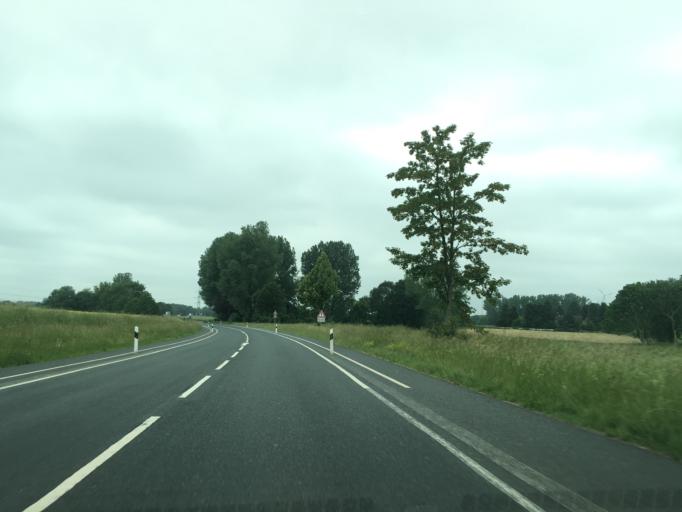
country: DE
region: North Rhine-Westphalia
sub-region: Regierungsbezirk Munster
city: Altenberge
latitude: 52.0486
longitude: 7.4304
